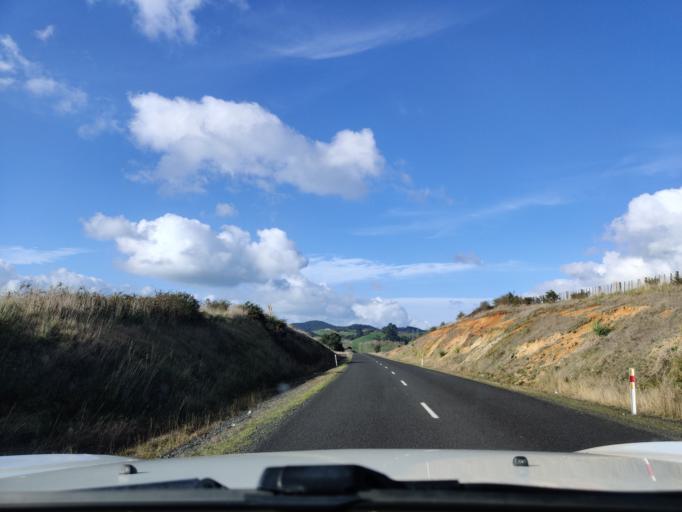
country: NZ
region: Waikato
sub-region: Waikato District
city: Te Kauwhata
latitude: -37.2831
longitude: 175.2020
